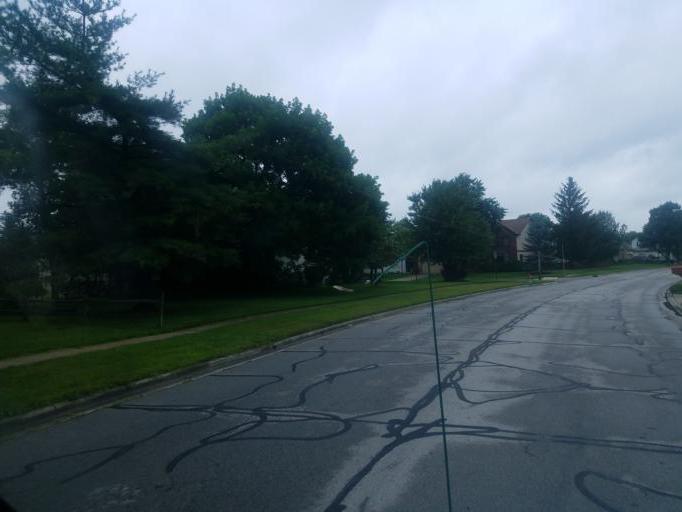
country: US
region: Ohio
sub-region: Franklin County
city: Gahanna
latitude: 40.0067
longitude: -82.8511
